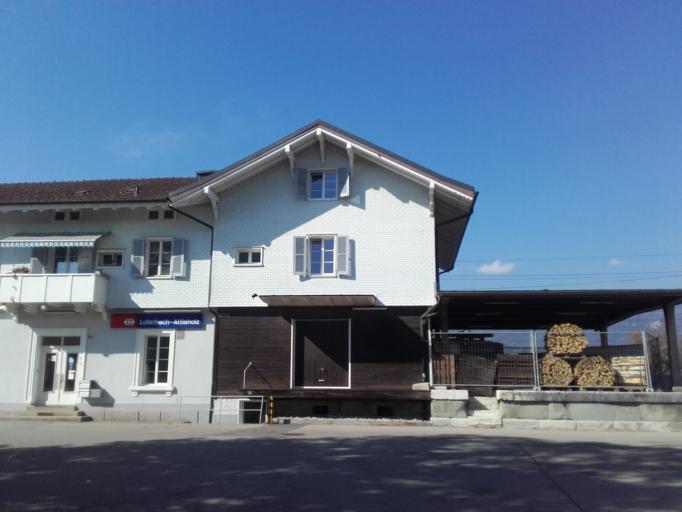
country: CH
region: Solothurn
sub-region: Bezirk Wasseramt
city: Luterbach
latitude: 47.2170
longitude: 7.5839
